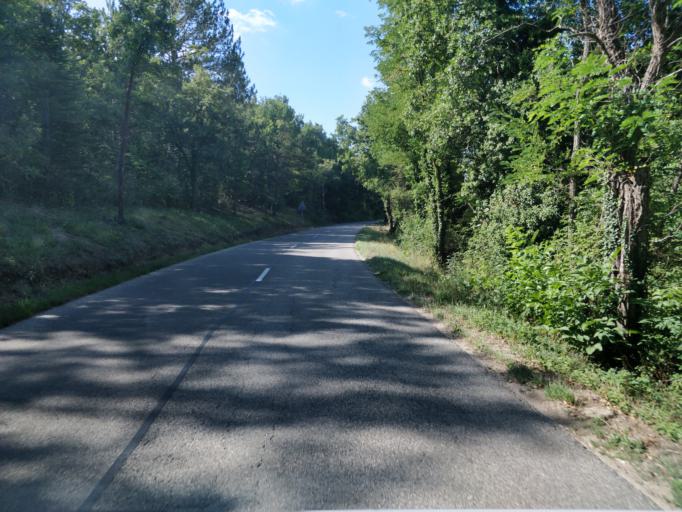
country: FR
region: Provence-Alpes-Cote d'Azur
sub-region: Departement des Alpes-de-Haute-Provence
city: Riez
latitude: 43.8303
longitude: 6.1398
